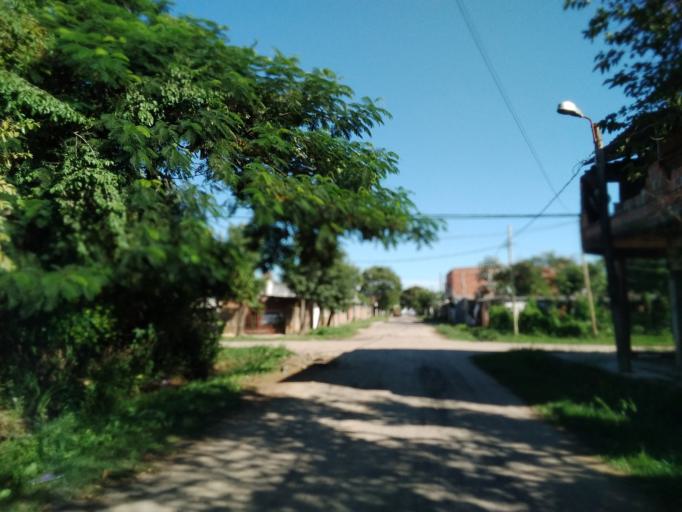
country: AR
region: Corrientes
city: Corrientes
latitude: -27.4846
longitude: -58.8035
